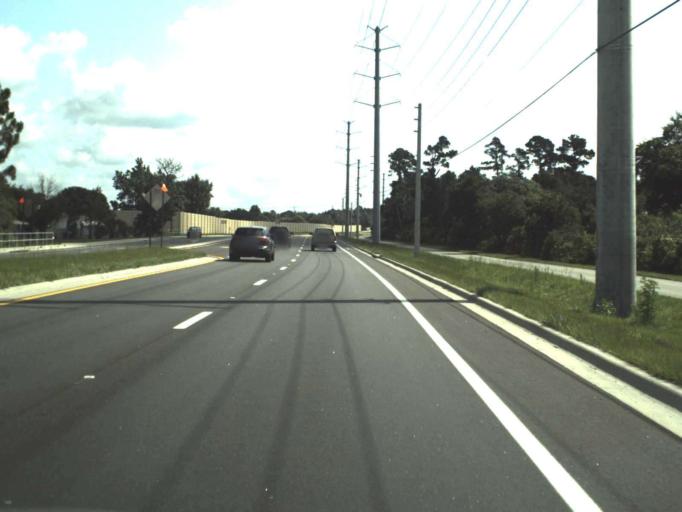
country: US
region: Florida
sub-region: Seminole County
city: Midway
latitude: 28.8331
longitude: -81.1740
